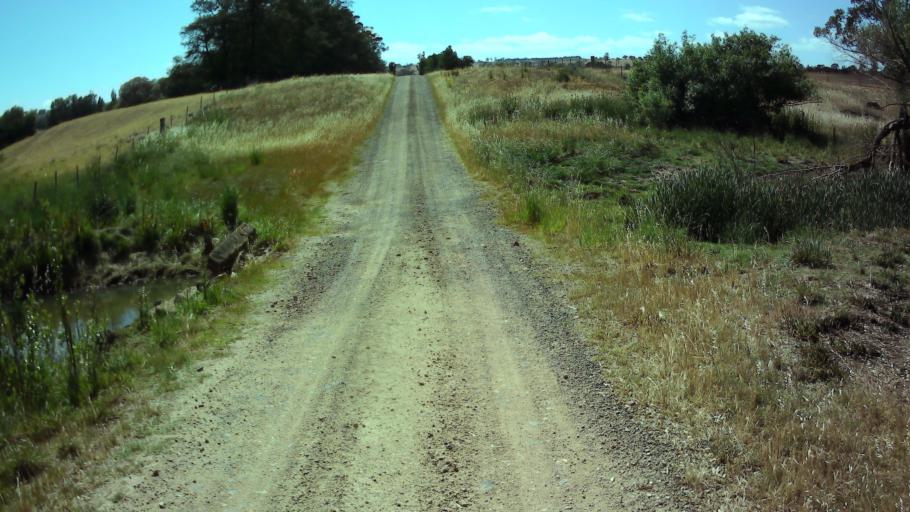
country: AU
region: New South Wales
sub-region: Weddin
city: Grenfell
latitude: -33.9571
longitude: 148.4327
